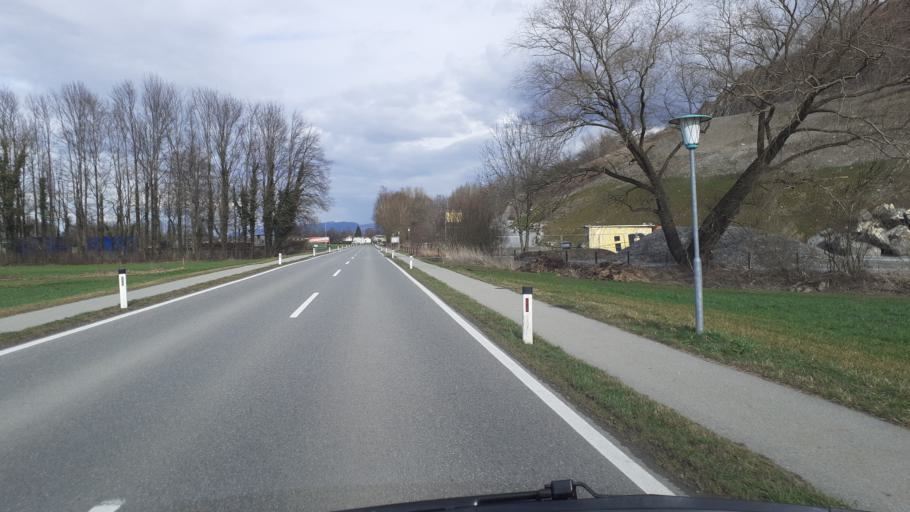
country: AT
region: Vorarlberg
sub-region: Politischer Bezirk Feldkirch
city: Koblach
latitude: 47.3404
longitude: 9.6014
